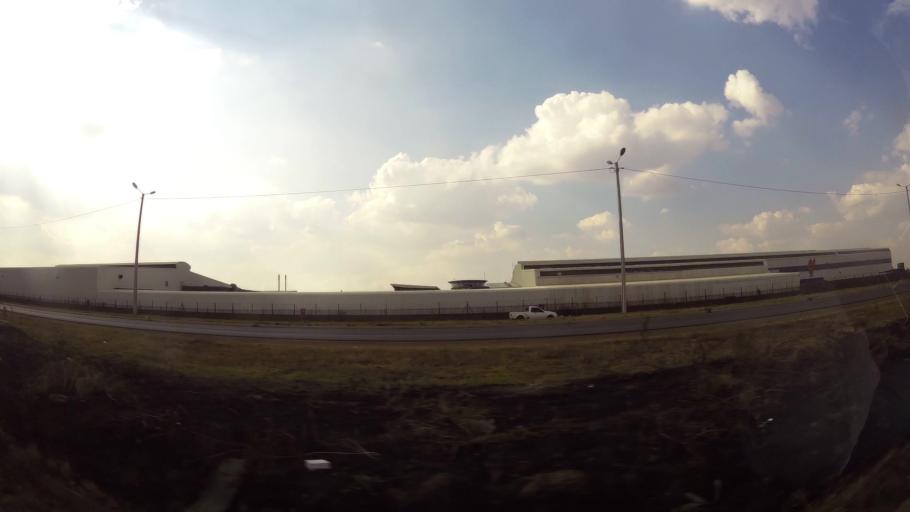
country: ZA
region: Gauteng
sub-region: Ekurhuleni Metropolitan Municipality
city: Germiston
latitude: -26.3098
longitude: 28.1996
